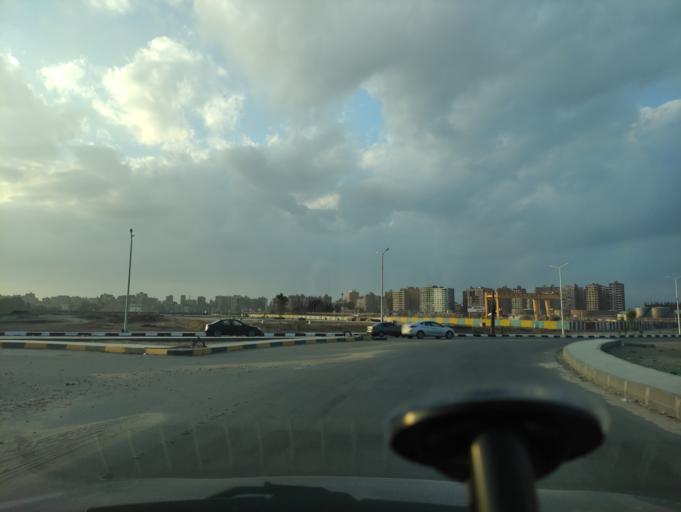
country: EG
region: Muhafazat al Qalyubiyah
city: Al Khankah
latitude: 30.1220
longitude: 31.3614
